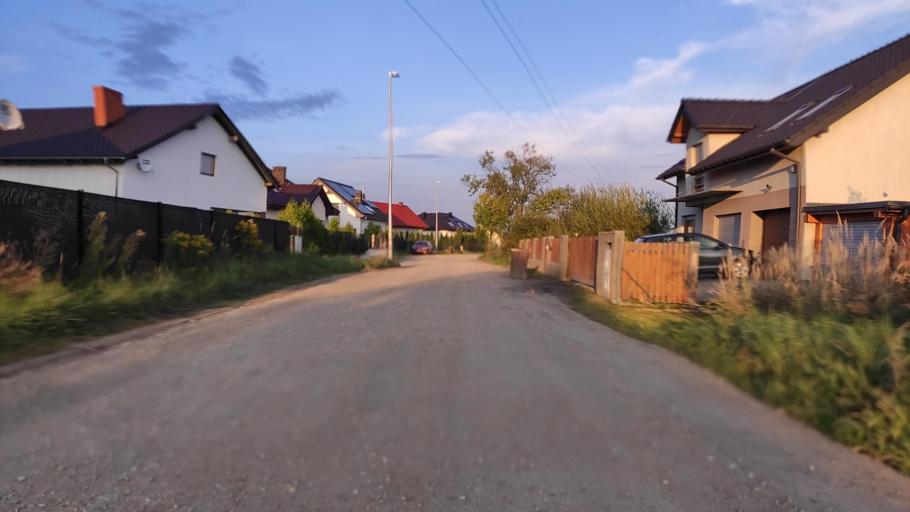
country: PL
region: Greater Poland Voivodeship
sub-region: Powiat poznanski
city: Kleszczewo
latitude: 52.3903
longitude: 17.1620
